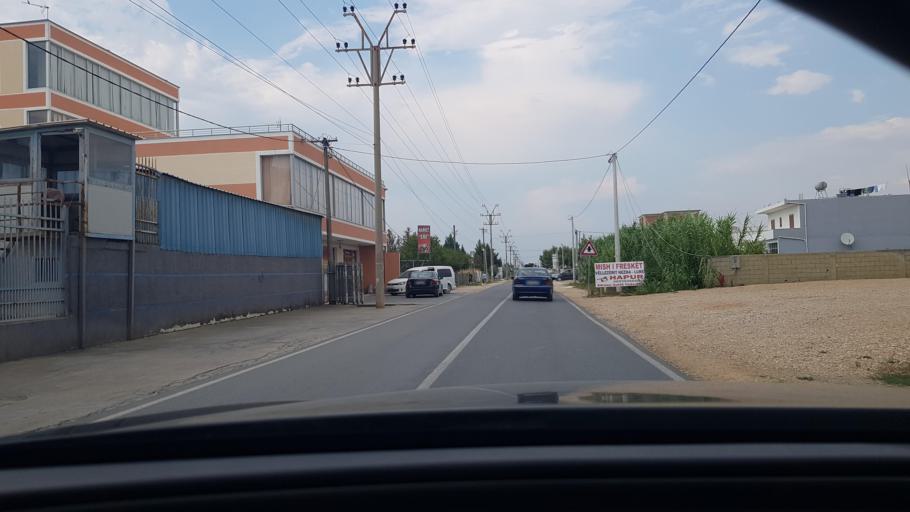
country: AL
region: Durres
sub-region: Rrethi i Durresit
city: Sukth
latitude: 41.3984
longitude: 19.5466
